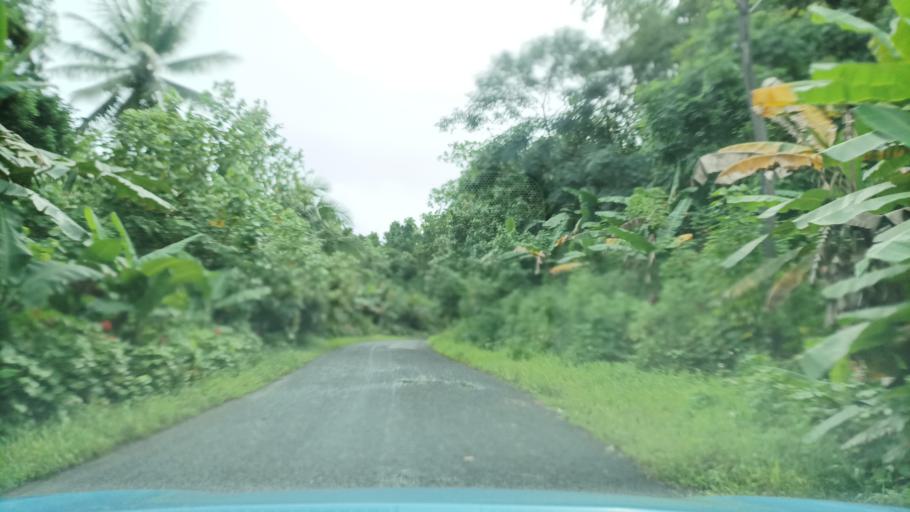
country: FM
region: Pohnpei
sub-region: Sokehs Municipality
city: Palikir - National Government Center
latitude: 6.8218
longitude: 158.1608
